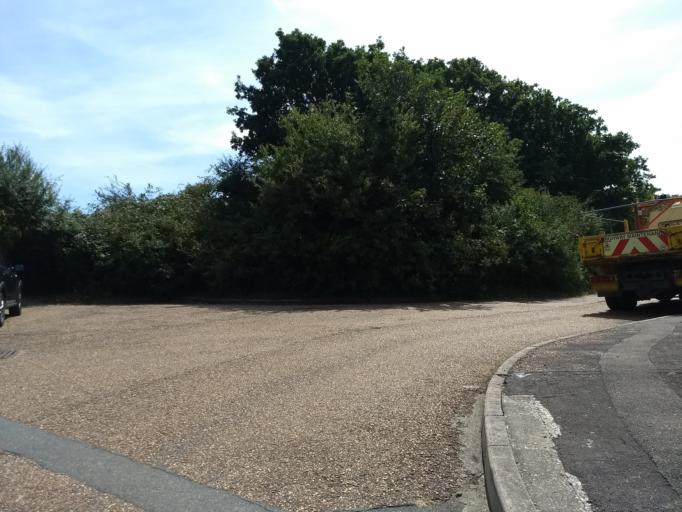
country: GB
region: England
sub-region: Isle of Wight
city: Gurnard
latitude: 50.7619
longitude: -1.3203
